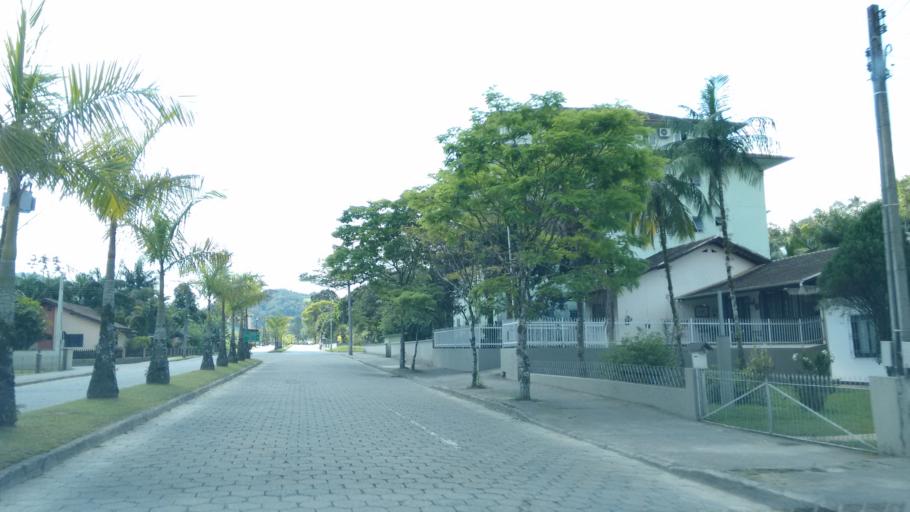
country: BR
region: Santa Catarina
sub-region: Pomerode
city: Pomerode
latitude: -26.7279
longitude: -49.1793
